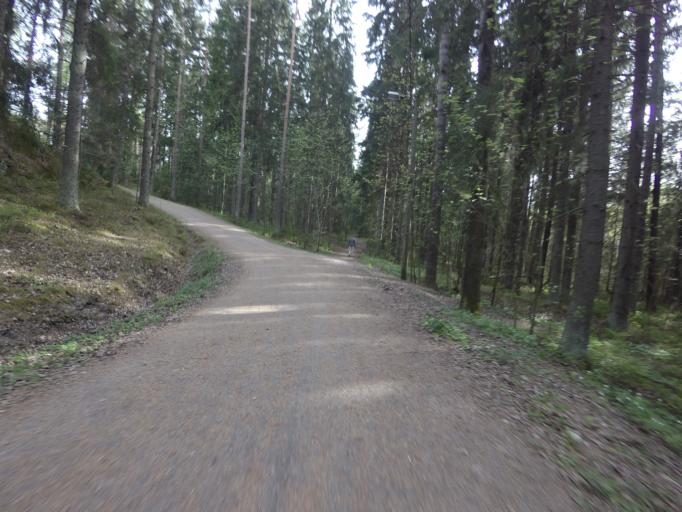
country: FI
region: Uusimaa
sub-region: Helsinki
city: Espoo
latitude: 60.1938
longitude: 24.6905
